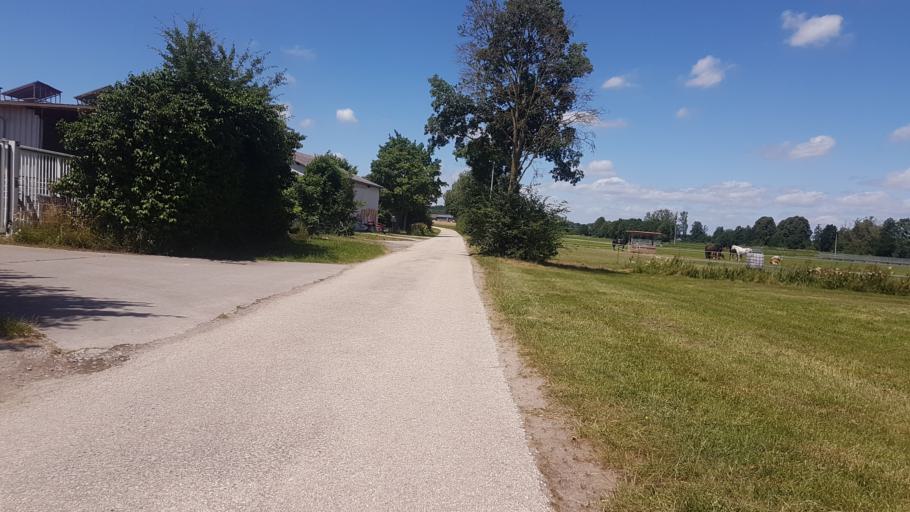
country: DE
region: Bavaria
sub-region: Regierungsbezirk Mittelfranken
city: Leutershausen
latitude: 49.2958
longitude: 10.4069
